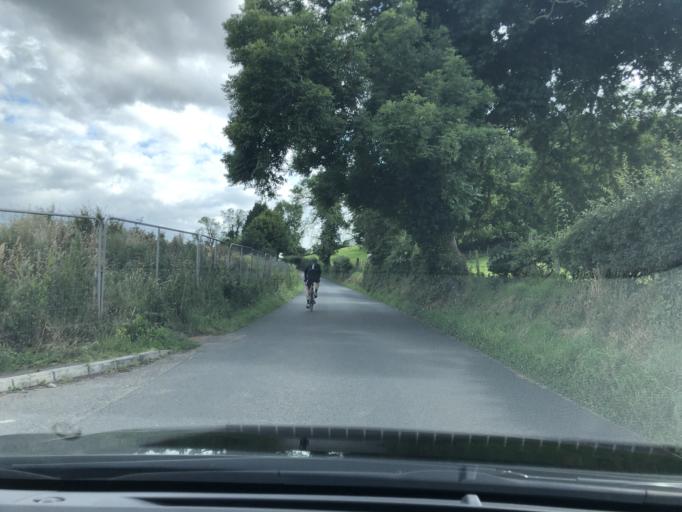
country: GB
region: Northern Ireland
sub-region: Ards District
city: Newtownards
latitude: 54.5841
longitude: -5.7123
